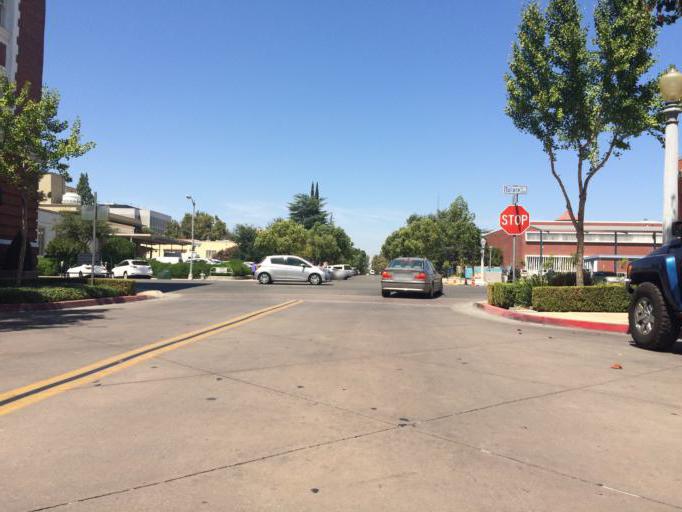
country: US
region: California
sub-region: Fresno County
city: Fresno
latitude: 36.7365
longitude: -119.7858
